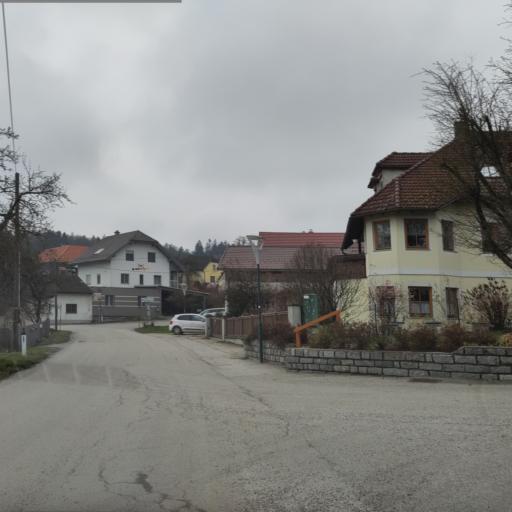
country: AT
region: Lower Austria
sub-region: Politischer Bezirk Sankt Polten
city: Hafnerbach
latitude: 48.2611
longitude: 15.4998
